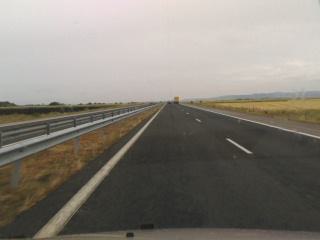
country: BG
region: Sliven
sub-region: Obshtina Nova Zagora
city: Nova Zagora
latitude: 42.4202
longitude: 25.9470
